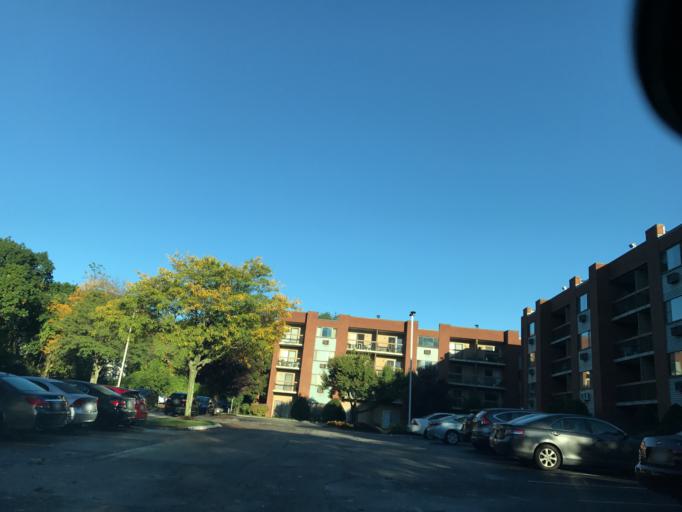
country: US
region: Massachusetts
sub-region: Norfolk County
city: Dedham
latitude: 42.2676
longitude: -71.1507
